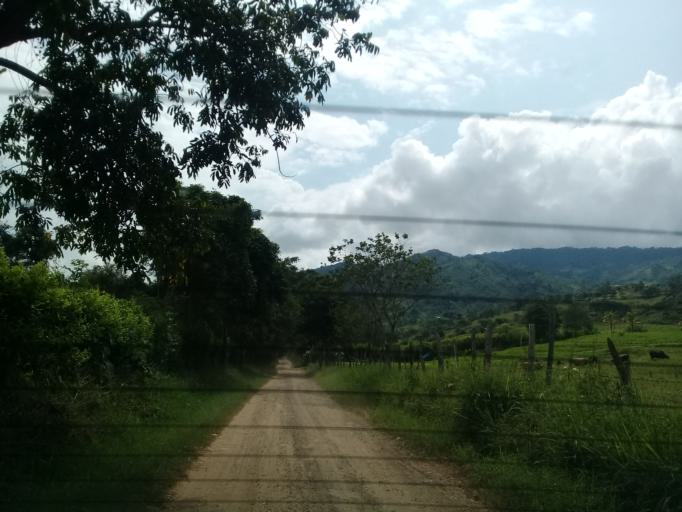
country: CO
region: Cundinamarca
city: Guaduas
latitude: 5.0282
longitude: -74.6076
